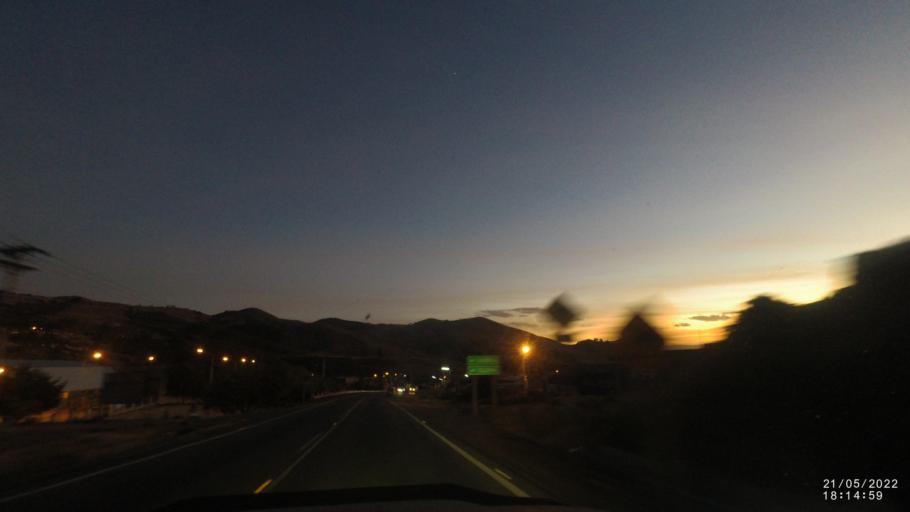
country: BO
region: Cochabamba
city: Colomi
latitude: -17.4247
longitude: -65.9152
